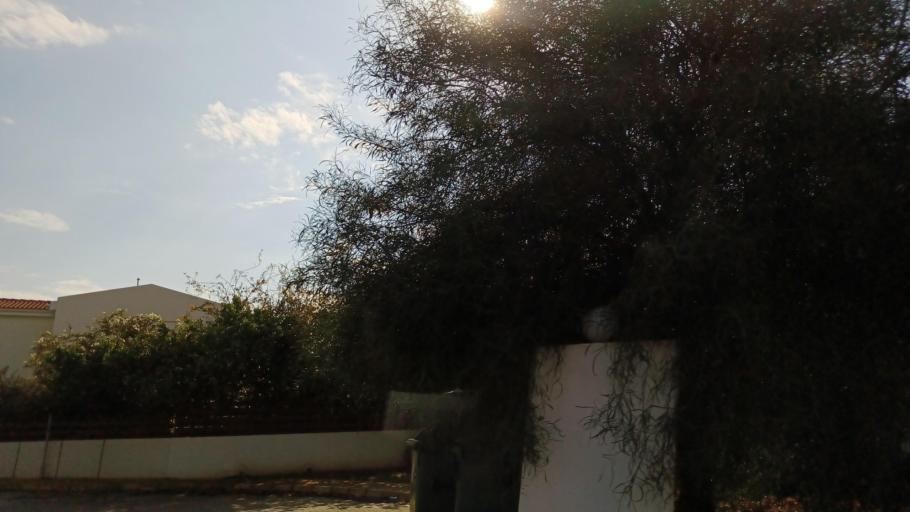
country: CY
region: Larnaka
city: Perivolia
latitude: 34.8236
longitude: 33.5745
